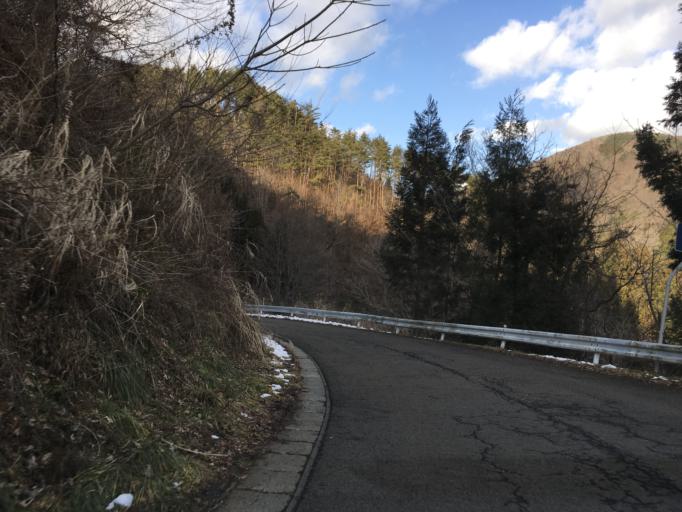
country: JP
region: Miyagi
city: Furukawa
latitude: 38.8131
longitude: 140.8327
